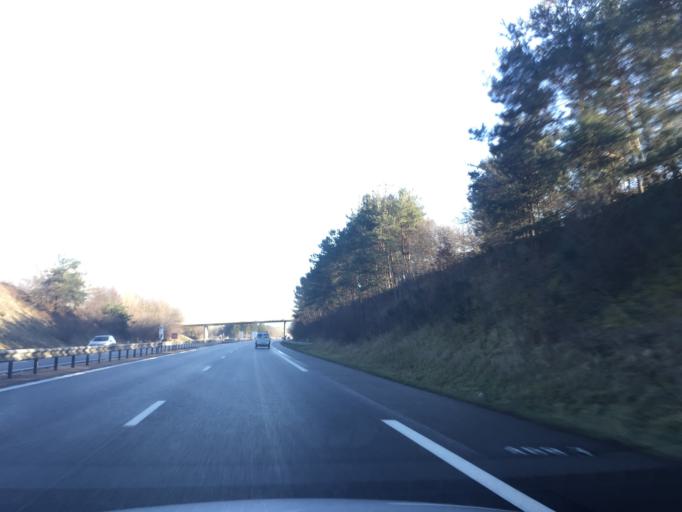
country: FR
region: Rhone-Alpes
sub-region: Departement de la Loire
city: Saint-Germain-Laval
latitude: 45.8693
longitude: 3.9495
